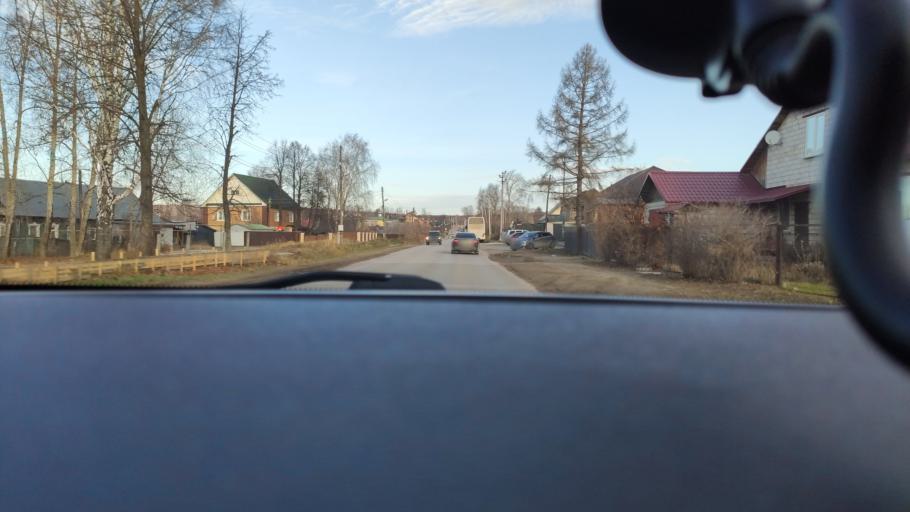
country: RU
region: Perm
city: Kondratovo
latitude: 58.0473
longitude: 56.0313
